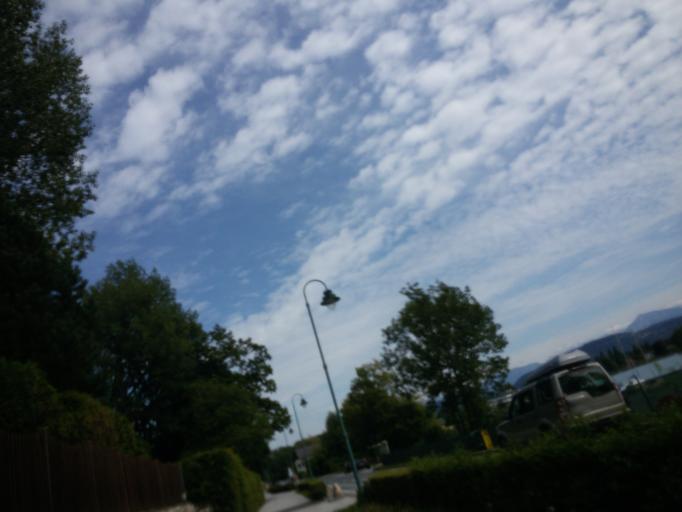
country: AT
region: Carinthia
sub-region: Politischer Bezirk Klagenfurt Land
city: Maria Worth
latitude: 46.6345
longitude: 14.1533
